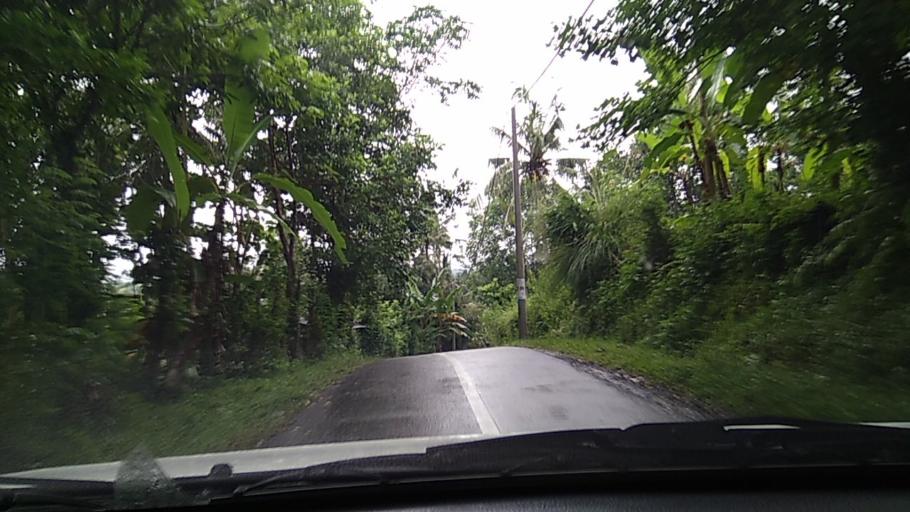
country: ID
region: Bali
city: Tiyingtali Kelod
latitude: -8.4086
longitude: 115.6224
